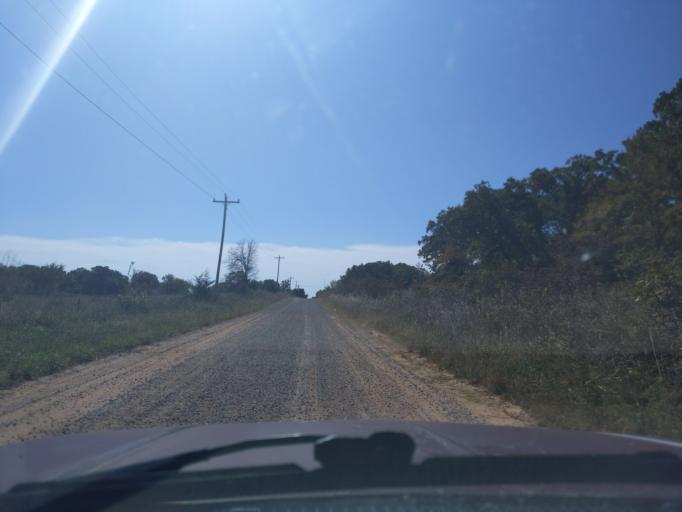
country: US
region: Oklahoma
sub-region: Okfuskee County
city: Boley
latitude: 35.6566
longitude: -96.4234
